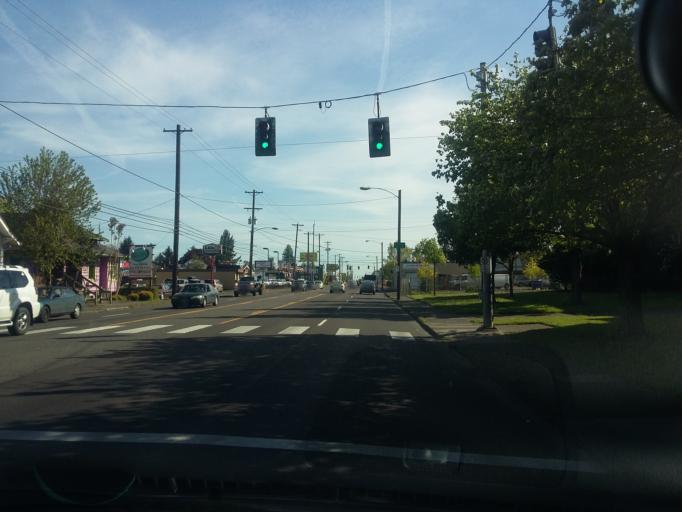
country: US
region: Oregon
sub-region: Multnomah County
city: Lents
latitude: 45.5248
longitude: -122.5792
